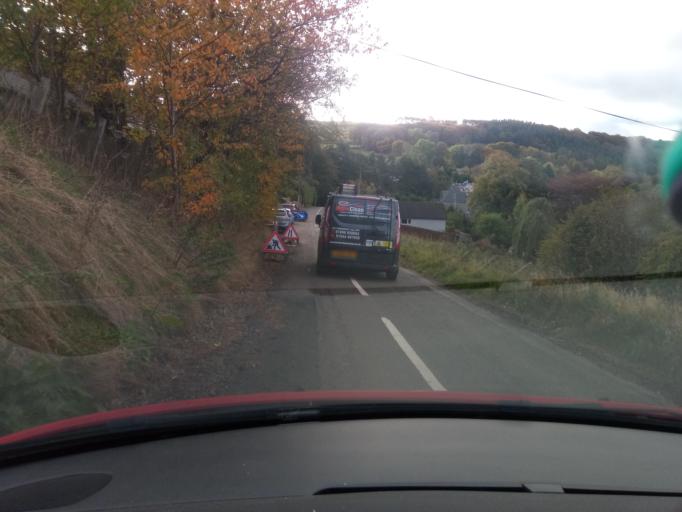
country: GB
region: Scotland
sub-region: The Scottish Borders
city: Galashiels
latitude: 55.6942
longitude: -2.8605
